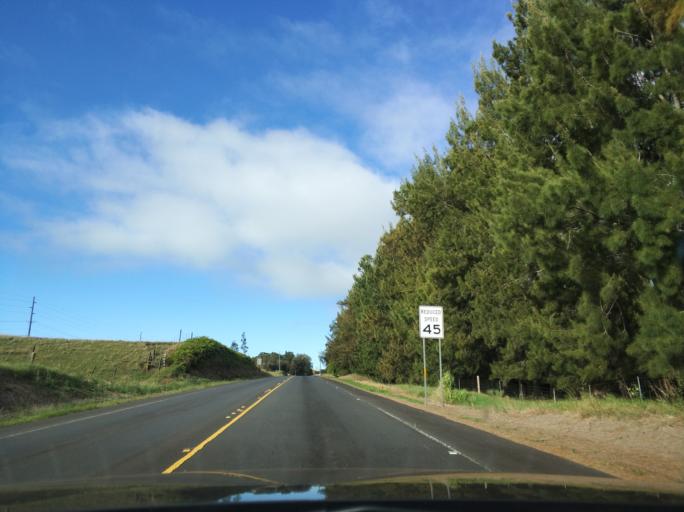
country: US
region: Hawaii
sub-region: Hawaii County
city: Waimea
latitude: 20.0439
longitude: -155.5931
